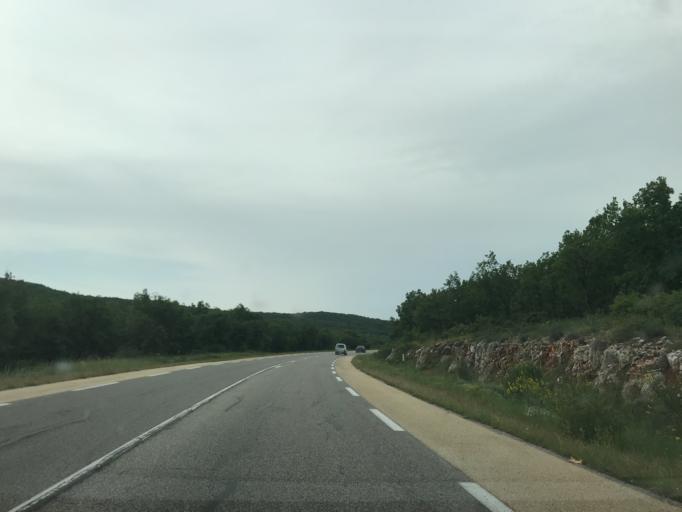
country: FR
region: Provence-Alpes-Cote d'Azur
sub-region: Departement du Var
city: Pourrieres
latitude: 43.5399
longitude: 5.8115
